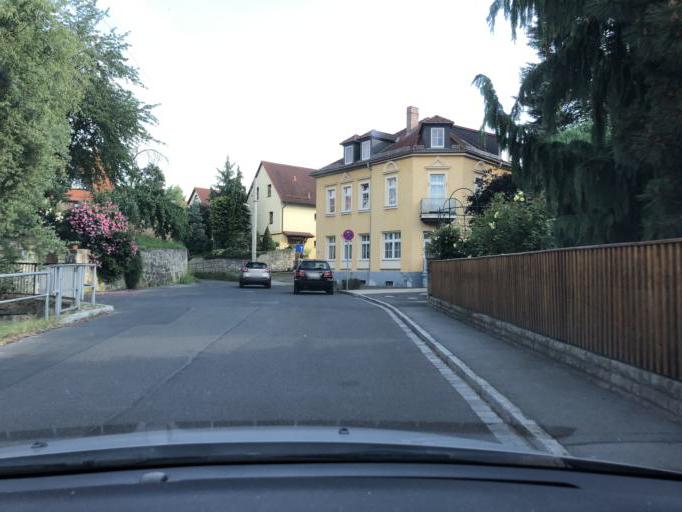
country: DE
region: Saxony
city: Kreischa
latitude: 50.9943
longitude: 13.7884
